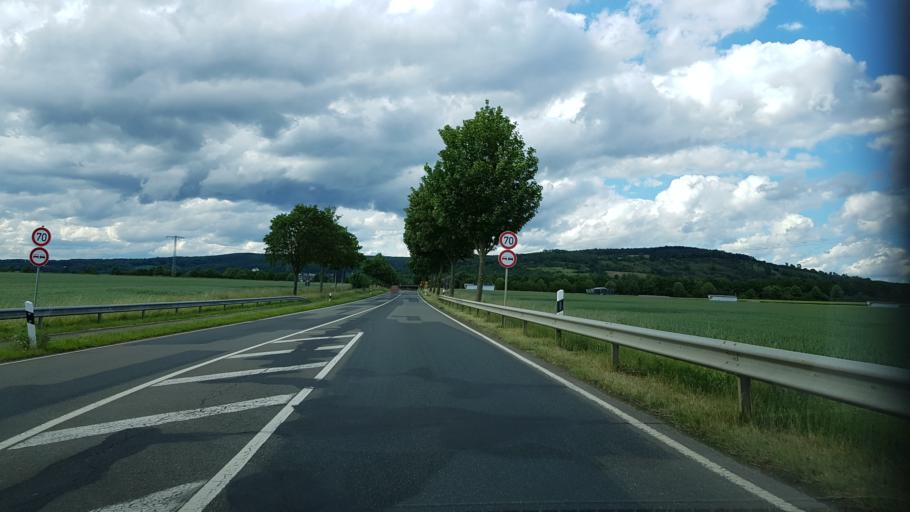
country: DE
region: Lower Saxony
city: Einbeck
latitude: 51.7998
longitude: 9.8982
